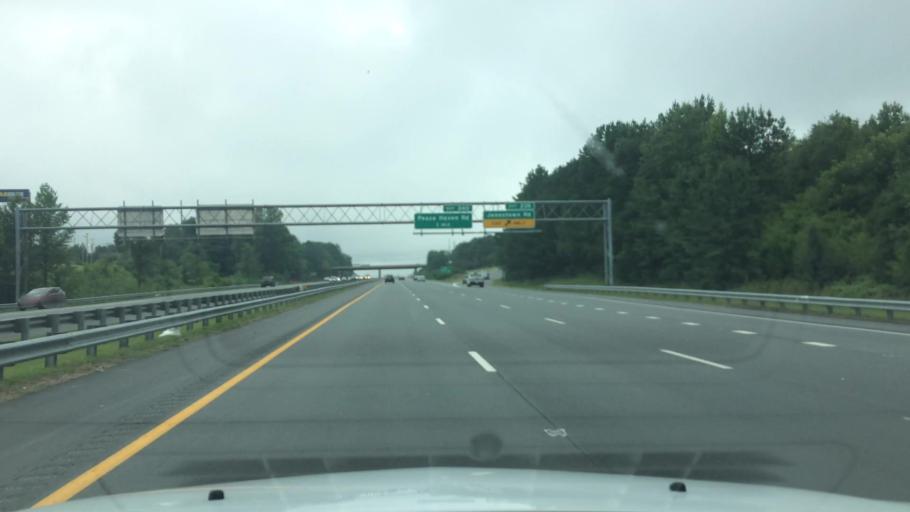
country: US
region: North Carolina
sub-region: Forsyth County
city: Clemmons
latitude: 36.0722
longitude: -80.3330
